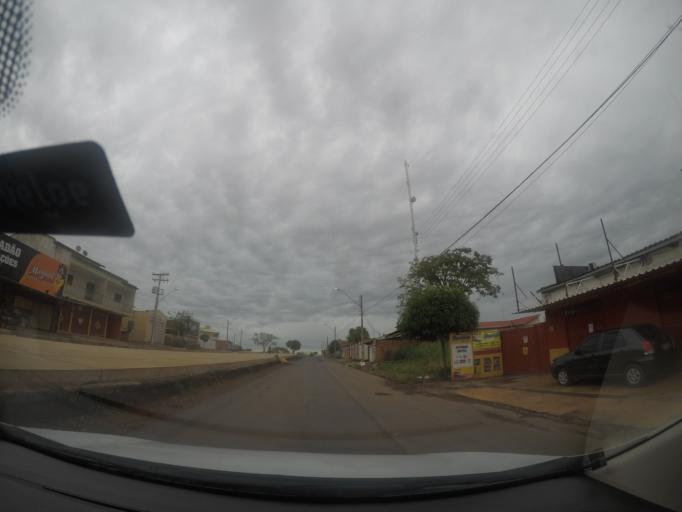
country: BR
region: Goias
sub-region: Goiania
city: Goiania
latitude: -16.6129
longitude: -49.3119
